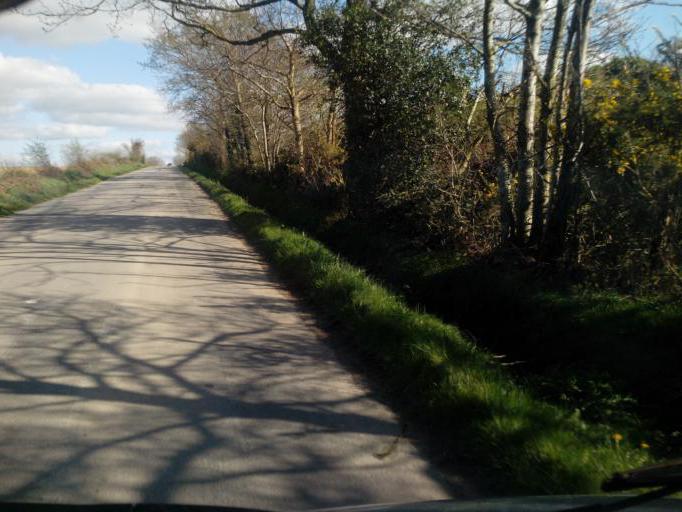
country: FR
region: Brittany
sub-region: Departement d'Ille-et-Vilaine
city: Messac
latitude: 47.7772
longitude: -1.7790
